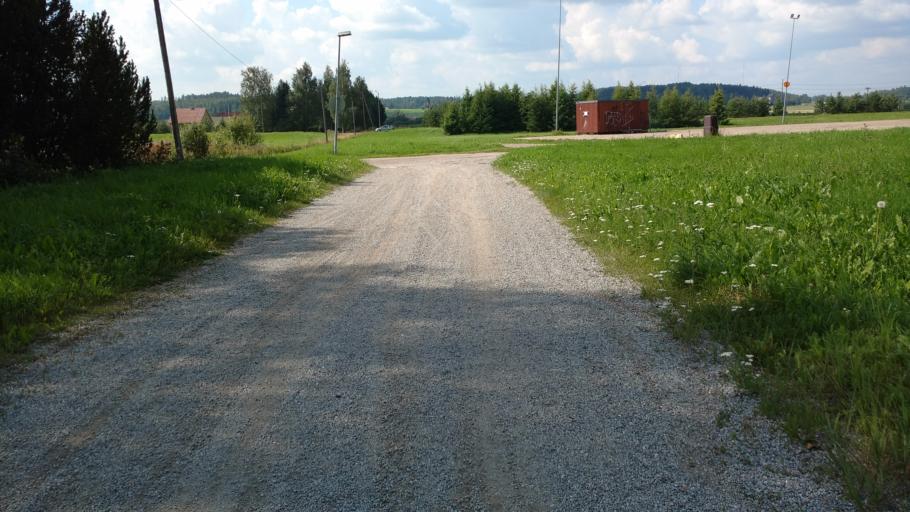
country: FI
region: Varsinais-Suomi
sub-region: Salo
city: Salo
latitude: 60.4047
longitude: 23.1738
